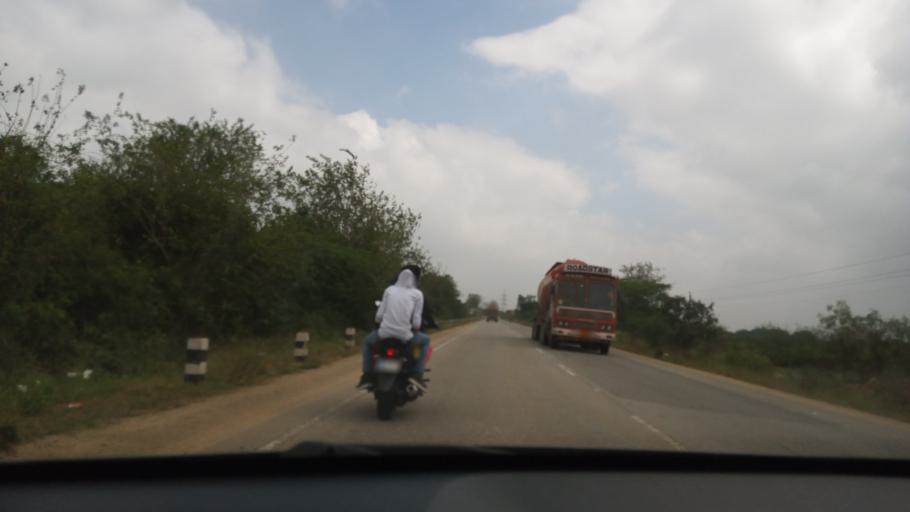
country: IN
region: Karnataka
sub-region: Chikkaballapur
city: Chintamani
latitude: 13.3674
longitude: 78.0550
